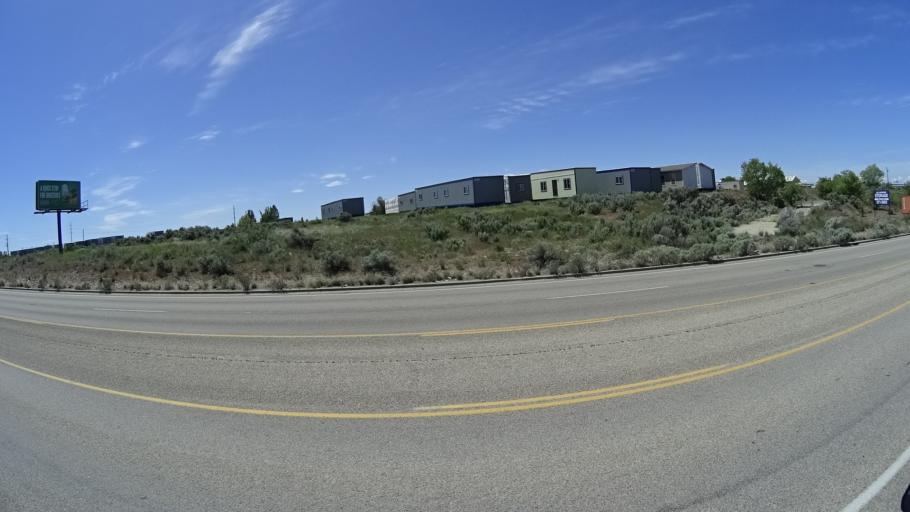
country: US
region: Idaho
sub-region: Ada County
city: Boise
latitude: 43.5646
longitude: -116.1755
